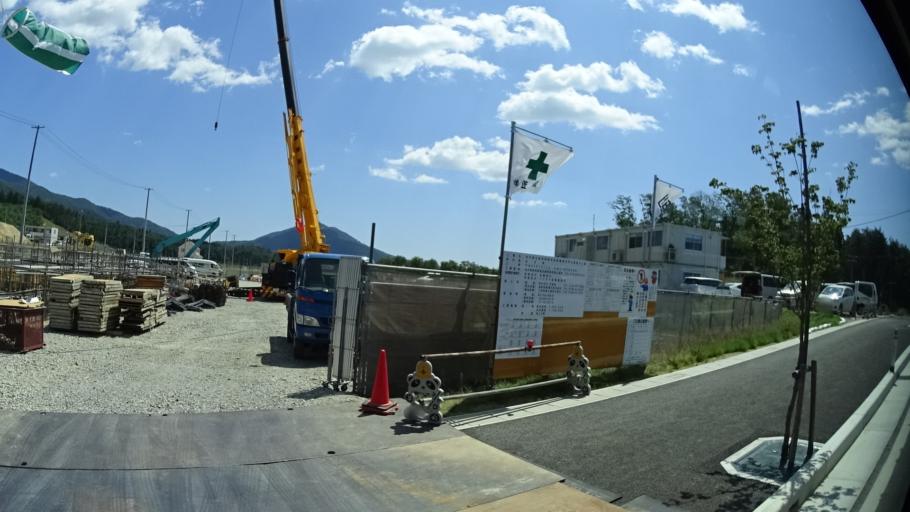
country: JP
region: Iwate
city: Ofunato
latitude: 39.0235
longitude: 141.6400
